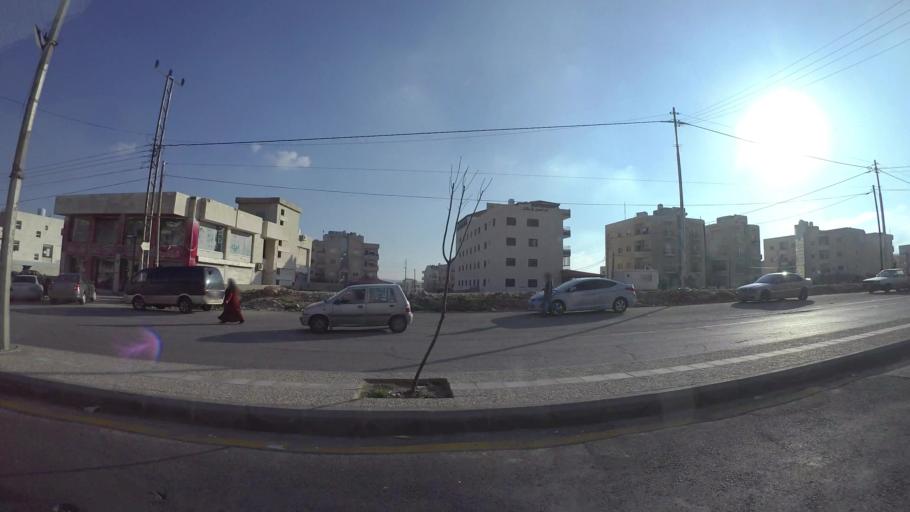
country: JO
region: Amman
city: Amman
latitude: 31.9799
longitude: 35.9414
